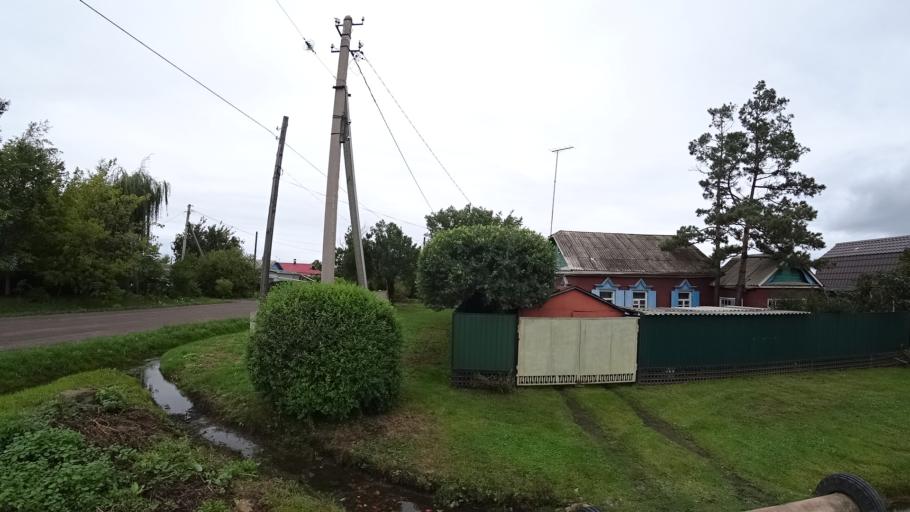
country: RU
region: Primorskiy
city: Chernigovka
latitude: 44.3417
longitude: 132.5648
